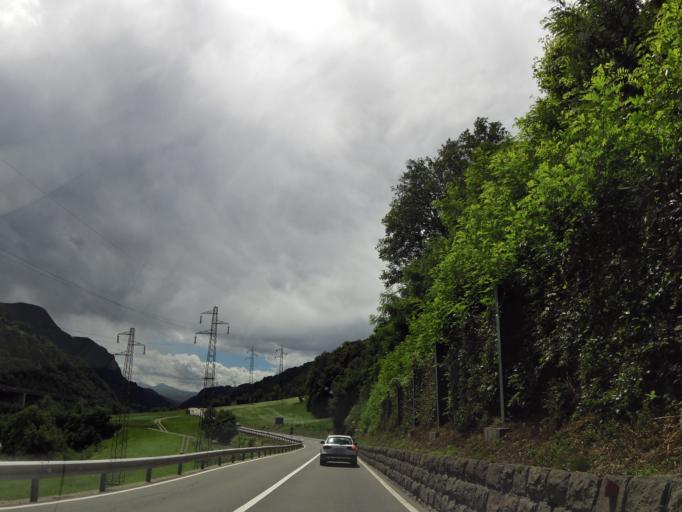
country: IT
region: Trentino-Alto Adige
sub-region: Bolzano
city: Villandro
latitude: 46.6185
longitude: 11.5388
